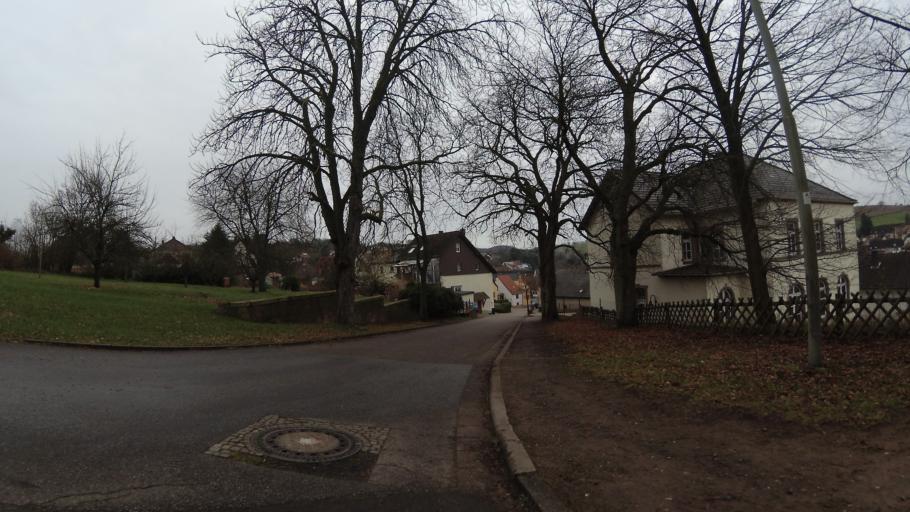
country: DE
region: Rheinland-Pfalz
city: Breitenbach
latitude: 49.4357
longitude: 7.2703
